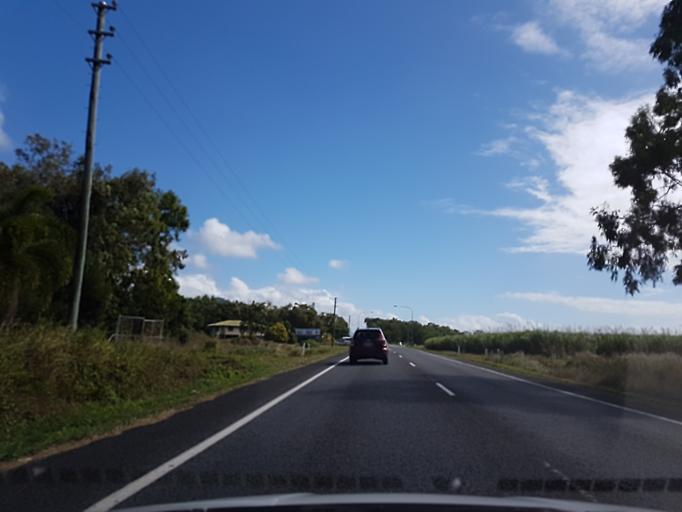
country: AU
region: Queensland
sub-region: Cairns
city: Port Douglas
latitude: -16.5503
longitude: 145.4742
